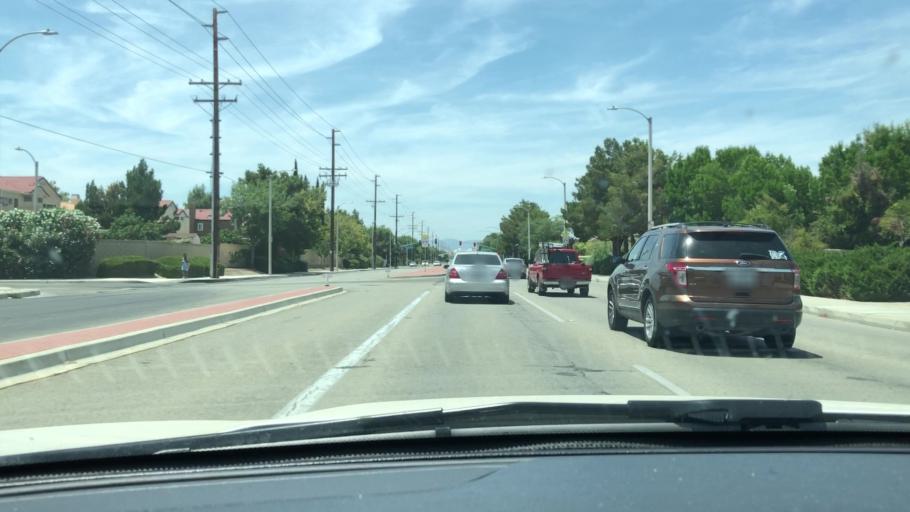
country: US
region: California
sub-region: Los Angeles County
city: Lancaster
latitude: 34.6894
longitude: -118.1768
